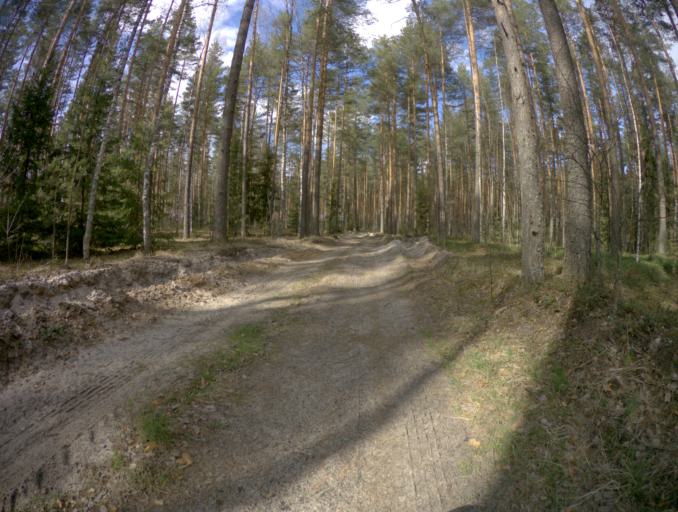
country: RU
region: Vladimir
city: Vorsha
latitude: 55.8813
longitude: 40.1766
